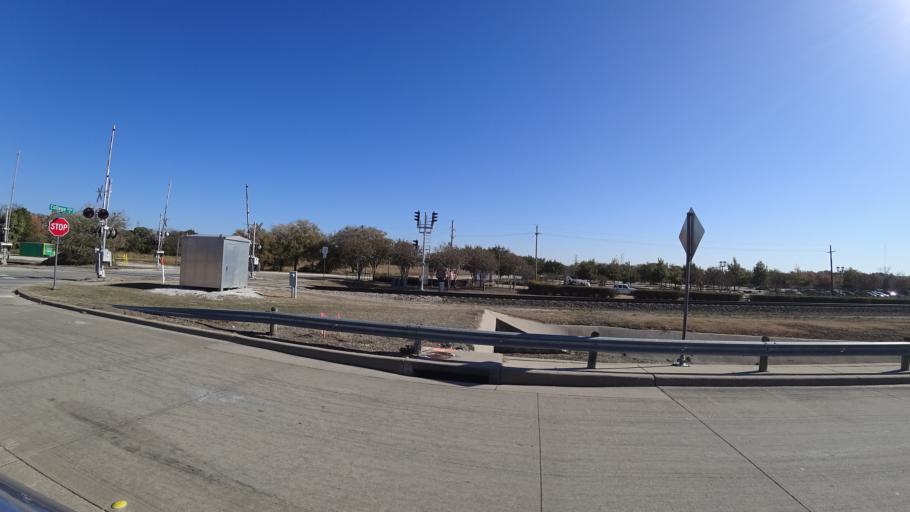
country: US
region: Texas
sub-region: Denton County
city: Lewisville
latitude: 33.0489
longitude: -96.9874
